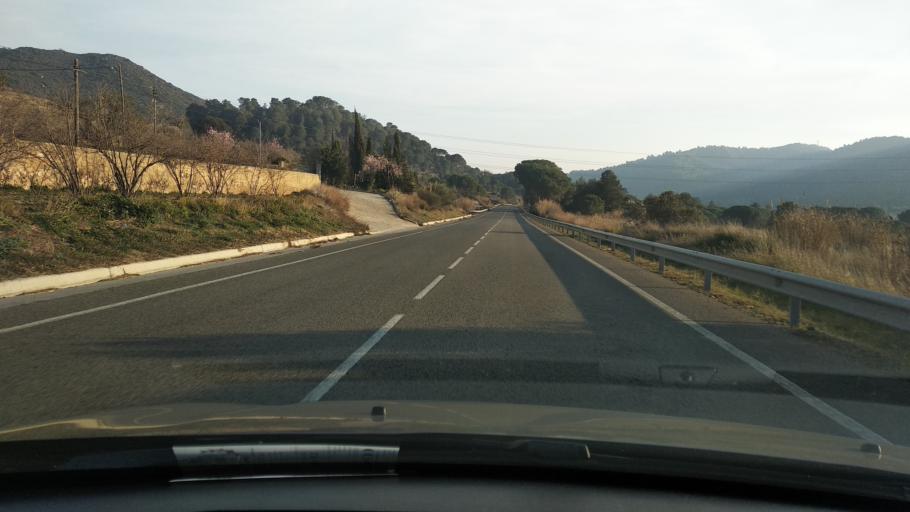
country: ES
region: Catalonia
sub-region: Provincia de Tarragona
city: Alforja
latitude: 41.2006
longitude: 0.9969
